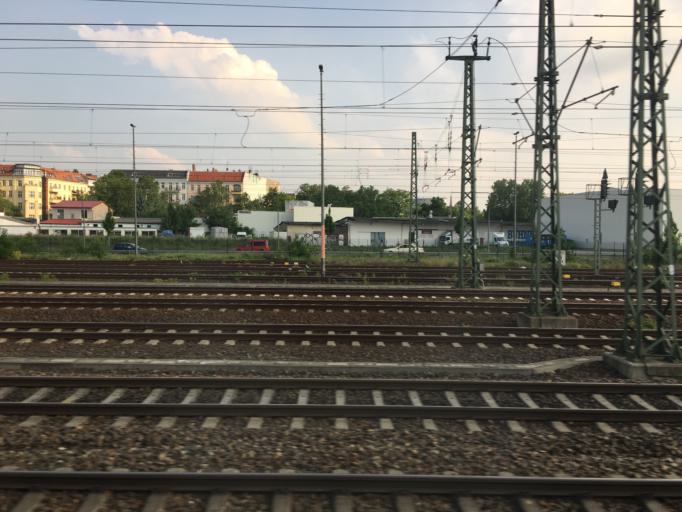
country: DE
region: Berlin
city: Moabit
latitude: 52.5354
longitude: 13.3393
